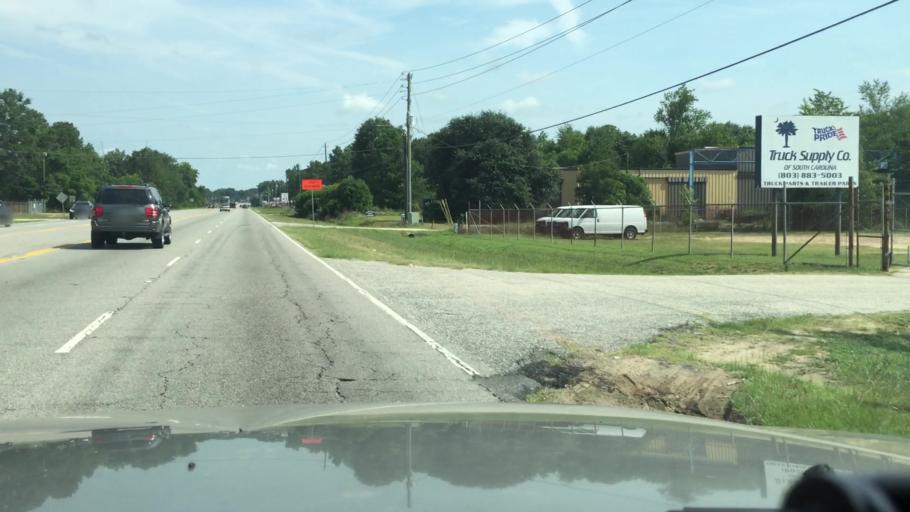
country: US
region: South Carolina
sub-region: Sumter County
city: South Sumter
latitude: 33.8896
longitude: -80.3510
